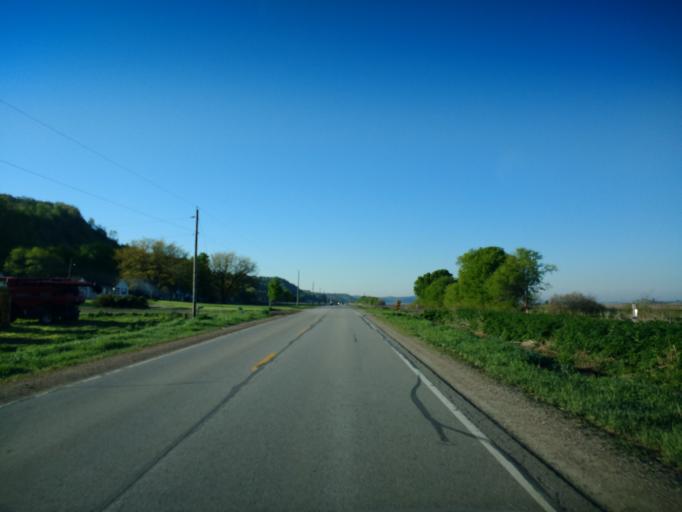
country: US
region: Iowa
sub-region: Harrison County
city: Missouri Valley
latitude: 41.4721
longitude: -95.8808
